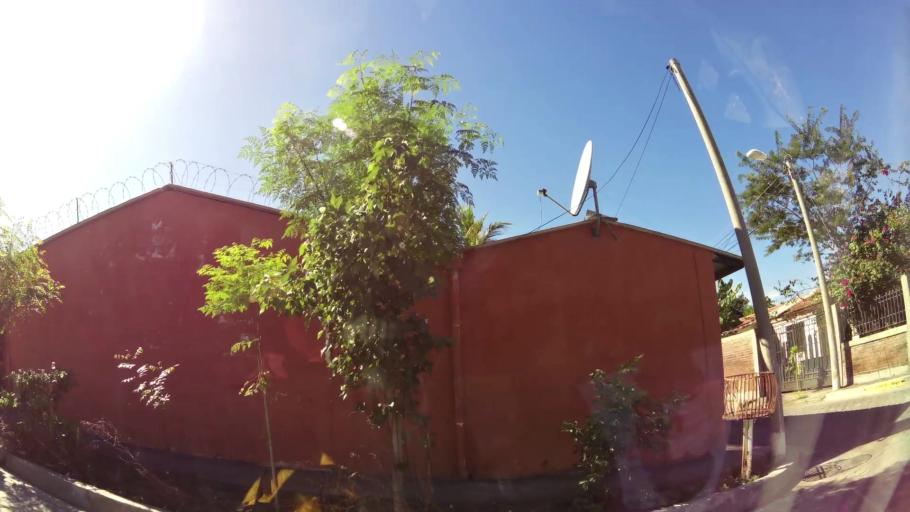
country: SV
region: San Miguel
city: San Miguel
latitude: 13.4714
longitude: -88.1558
